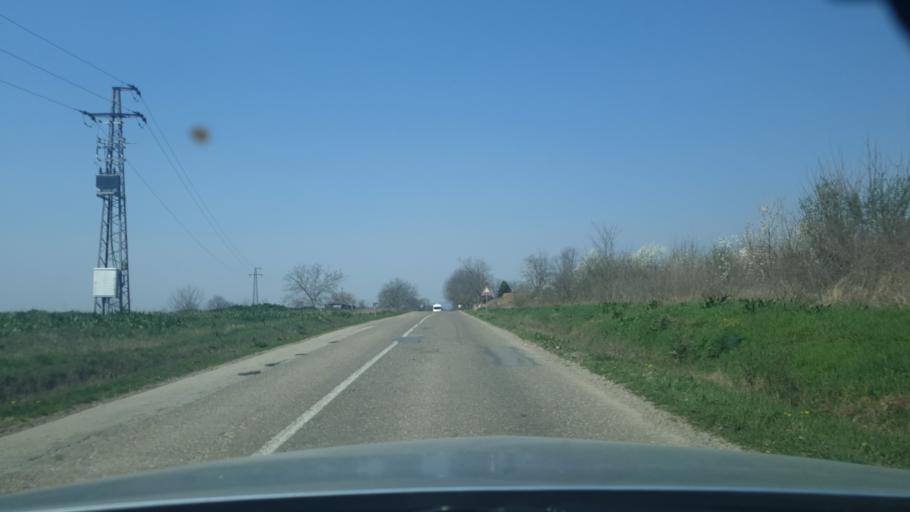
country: RS
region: Autonomna Pokrajina Vojvodina
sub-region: Sremski Okrug
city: Ruma
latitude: 45.0110
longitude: 19.7837
